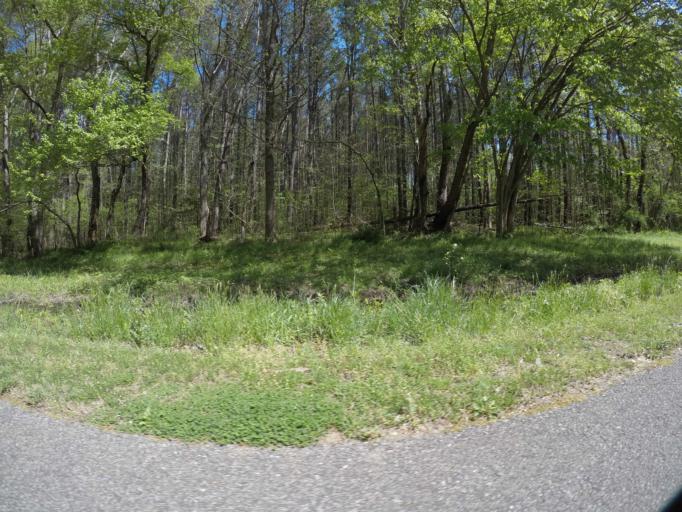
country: US
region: Maryland
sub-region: Charles County
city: Potomac Heights
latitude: 38.5867
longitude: -77.1026
